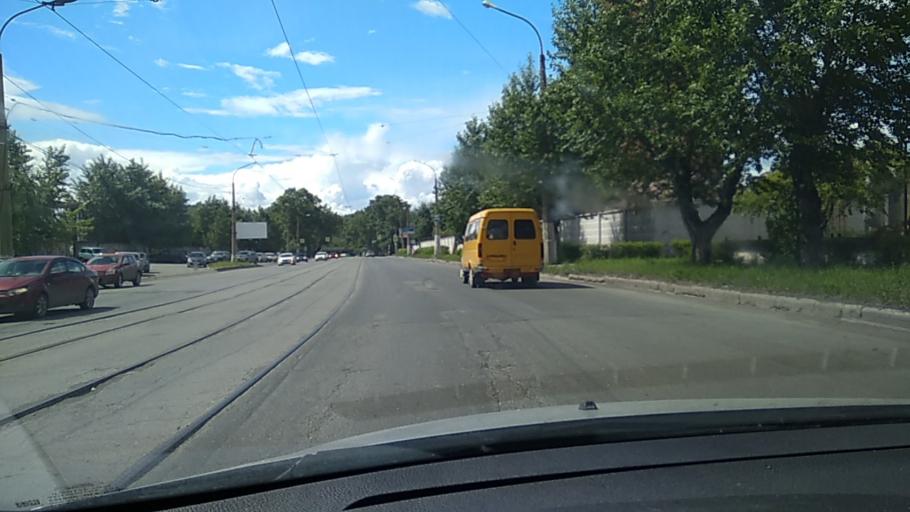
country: RU
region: Sverdlovsk
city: Nizhniy Tagil
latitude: 57.9297
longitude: 60.0053
